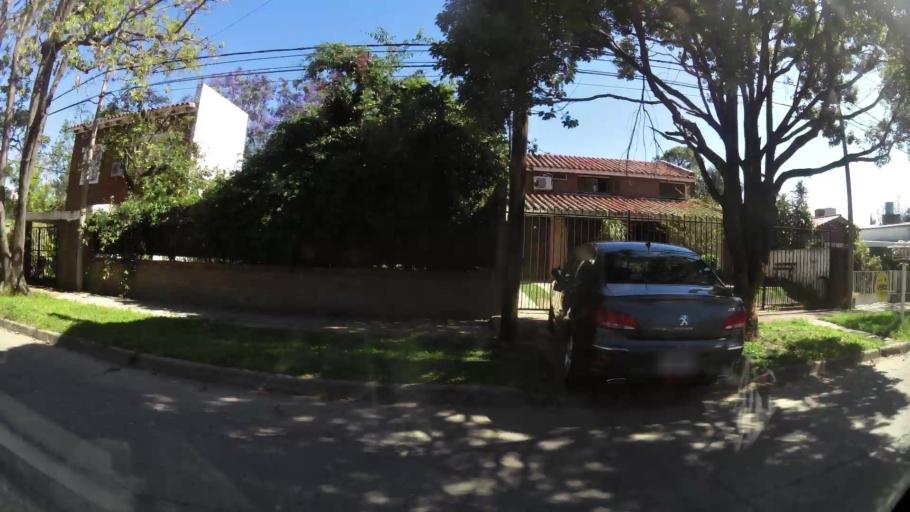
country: AR
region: Santa Fe
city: Santa Fe de la Vera Cruz
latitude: -31.6019
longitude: -60.6665
